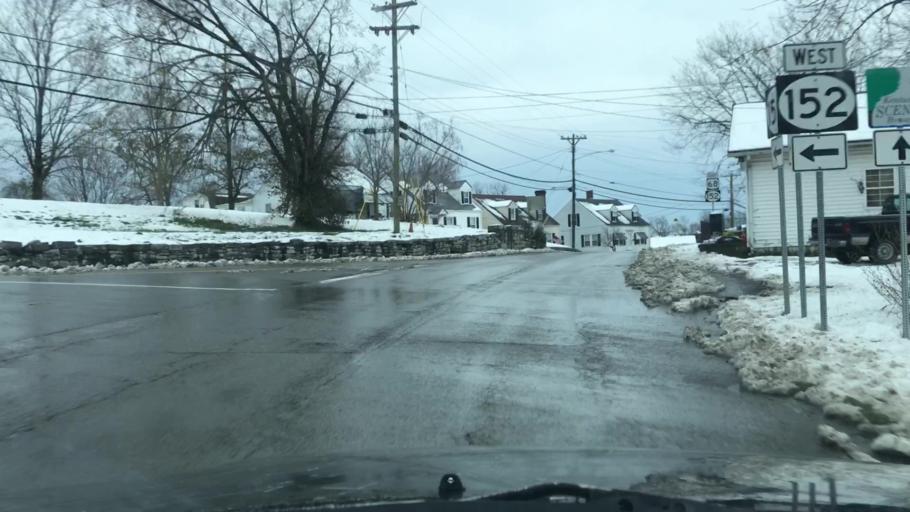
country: US
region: Kentucky
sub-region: Mercer County
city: Harrodsburg
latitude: 37.7583
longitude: -84.8498
